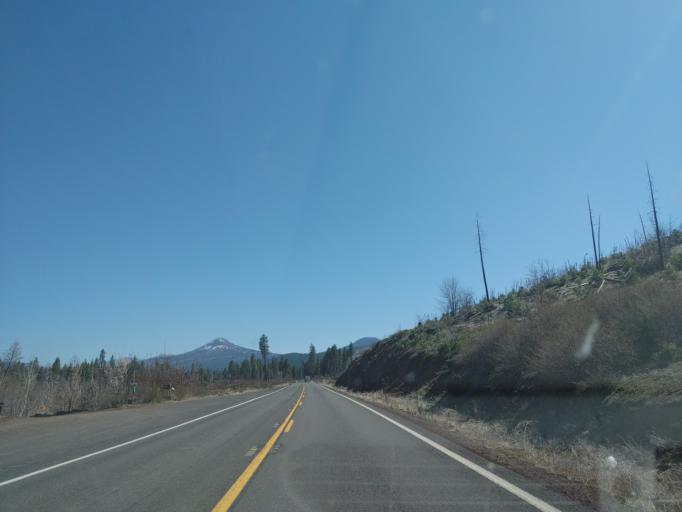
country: US
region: California
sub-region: Shasta County
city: Burney
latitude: 40.7895
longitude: -121.5063
